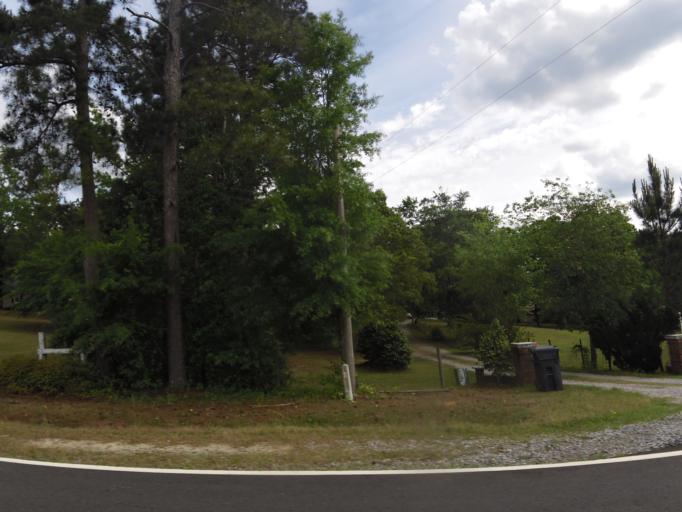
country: US
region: Georgia
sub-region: McDuffie County
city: Thomson
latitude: 33.5237
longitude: -82.4468
